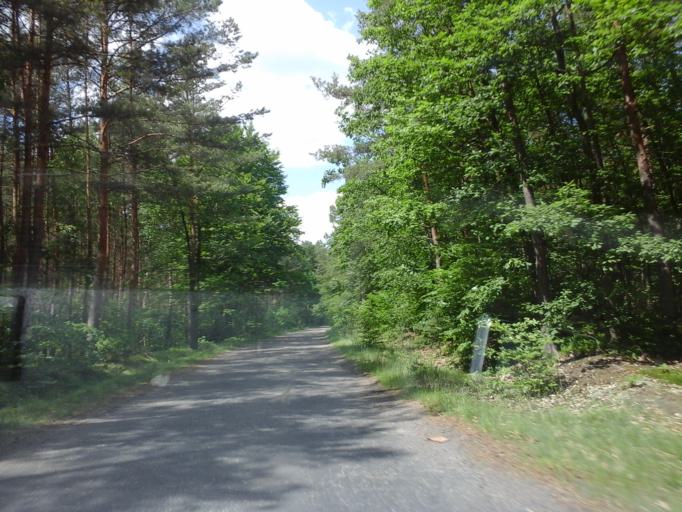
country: PL
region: West Pomeranian Voivodeship
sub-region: Powiat choszczenski
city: Bierzwnik
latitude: 53.0926
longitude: 15.7608
